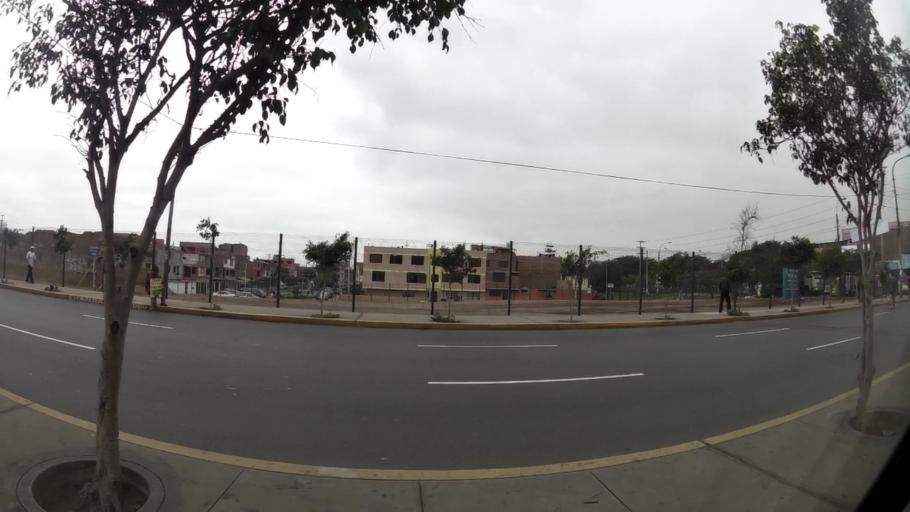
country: PE
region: Lima
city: Lima
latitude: -12.0639
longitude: -77.0600
